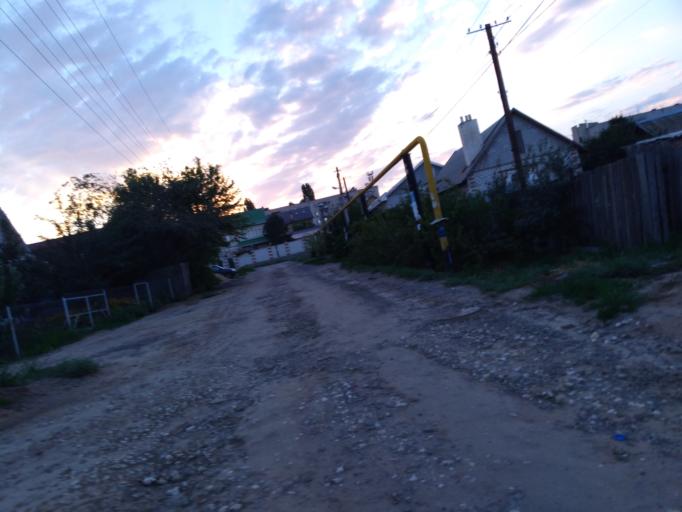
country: RU
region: Volgograd
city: Volgograd
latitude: 48.6701
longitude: 44.4514
